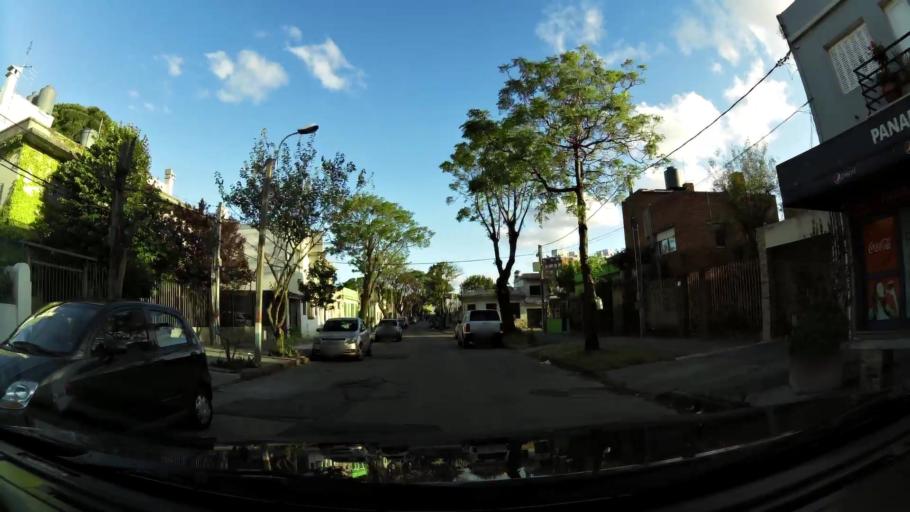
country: UY
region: Montevideo
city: Montevideo
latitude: -34.8828
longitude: -56.1481
